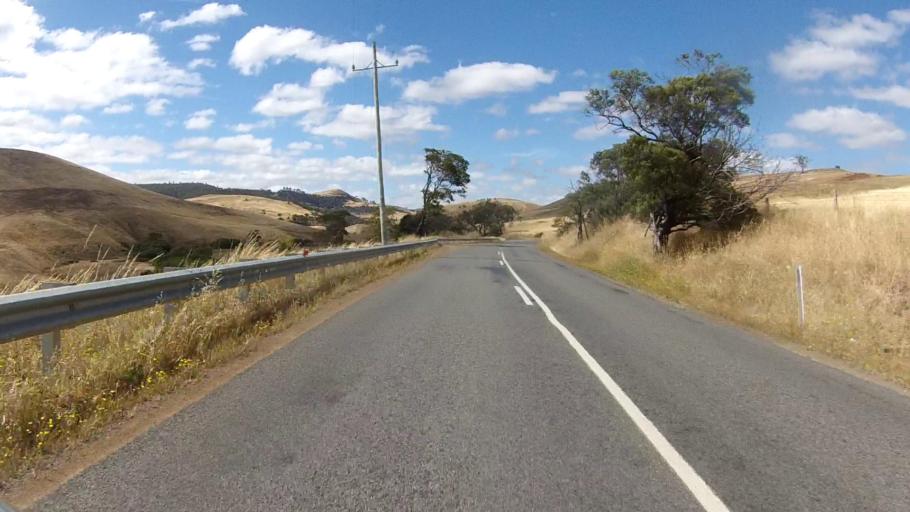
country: AU
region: Tasmania
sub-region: Brighton
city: Bridgewater
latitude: -42.5727
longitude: 147.3991
